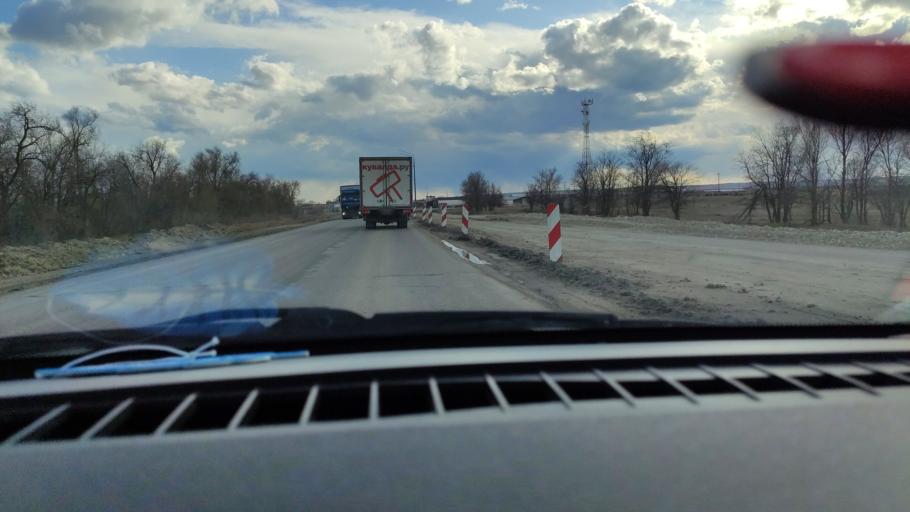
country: RU
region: Saratov
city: Sinodskoye
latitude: 51.9976
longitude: 46.6750
